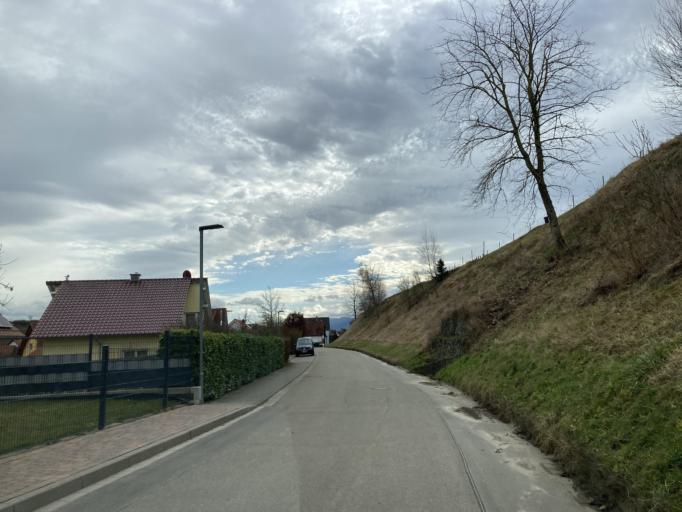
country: DE
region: Baden-Wuerttemberg
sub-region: Freiburg Region
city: Eichstetten
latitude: 48.0984
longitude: 7.7348
